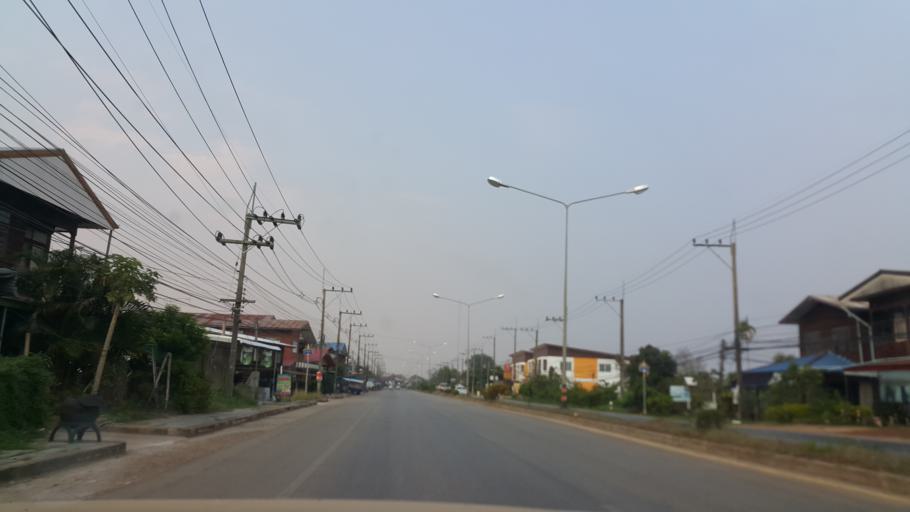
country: TH
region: Nakhon Phanom
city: That Phanom
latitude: 16.9677
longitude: 104.7274
